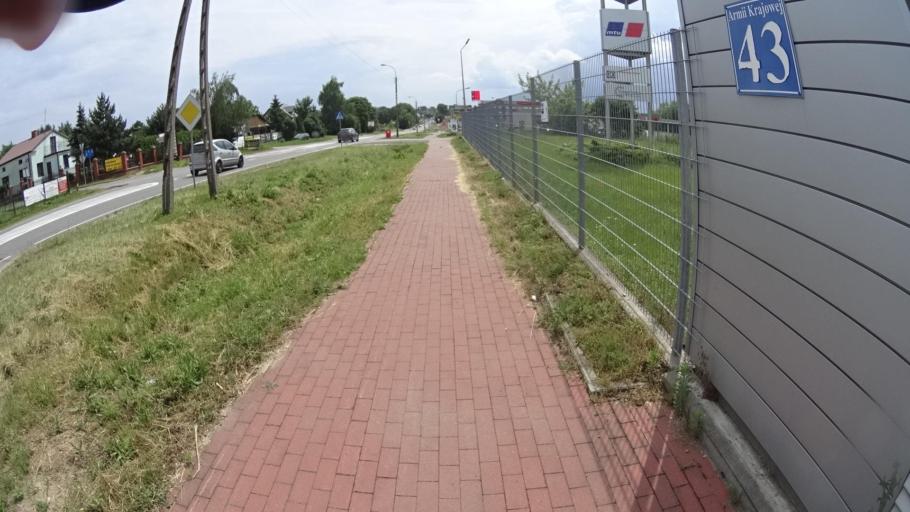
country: PL
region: Masovian Voivodeship
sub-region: Powiat grojecki
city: Grojec
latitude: 51.8786
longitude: 20.8639
